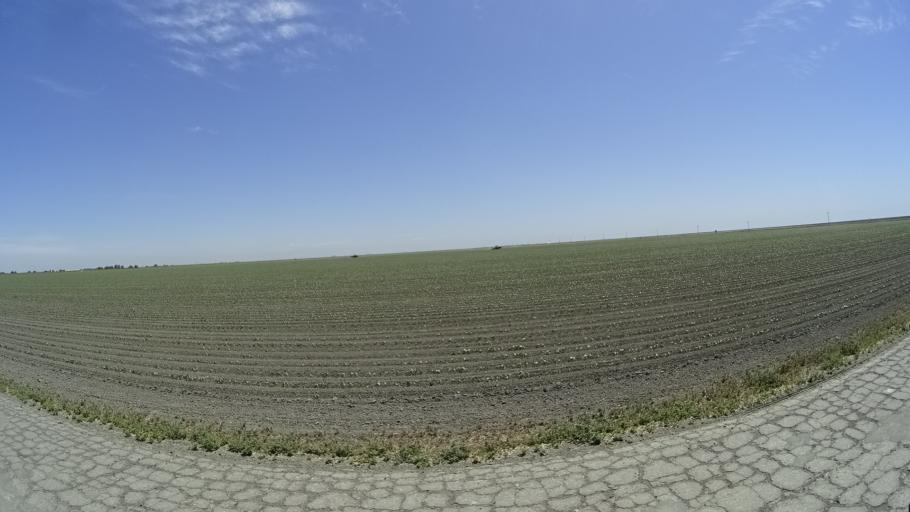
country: US
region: California
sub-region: Kings County
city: Stratford
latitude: 36.1259
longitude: -119.7340
